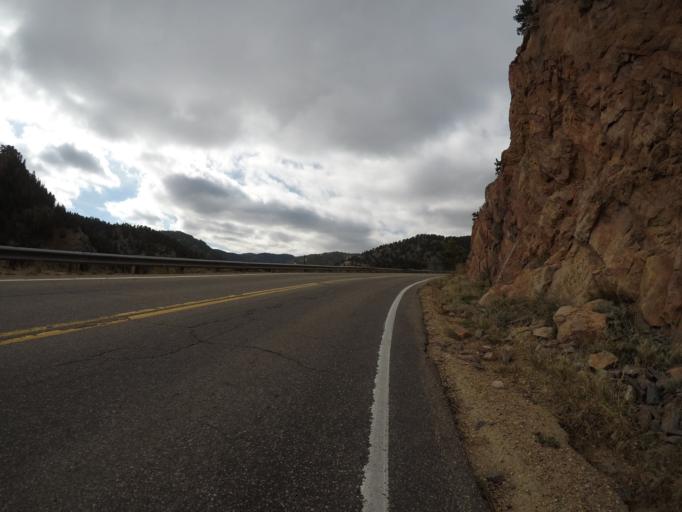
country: US
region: Colorado
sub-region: Boulder County
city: Boulder
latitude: 40.0655
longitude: -105.3059
